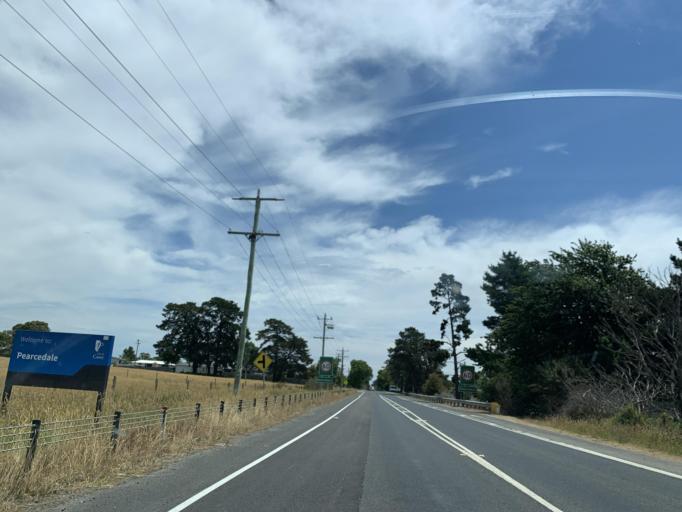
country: AU
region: Victoria
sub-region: Mornington Peninsula
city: Langwarrin South
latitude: -38.2038
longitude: 145.2425
